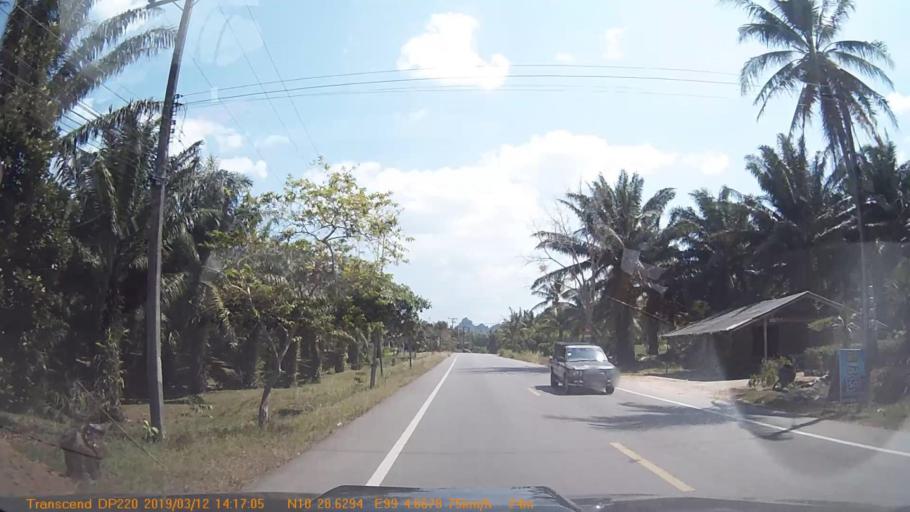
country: TH
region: Chumphon
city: Chumphon
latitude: 10.4768
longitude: 99.0778
